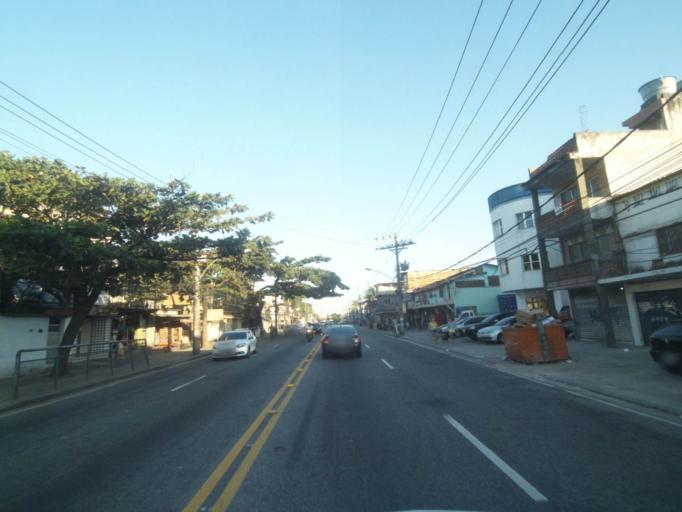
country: BR
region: Rio de Janeiro
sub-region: Sao Joao De Meriti
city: Sao Joao de Meriti
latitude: -22.9484
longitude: -43.3599
